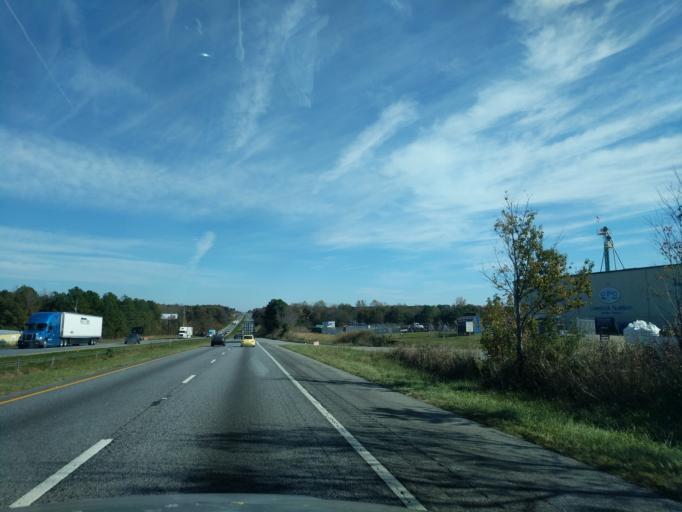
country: US
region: South Carolina
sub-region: Spartanburg County
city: Cowpens
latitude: 35.0453
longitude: -81.8132
